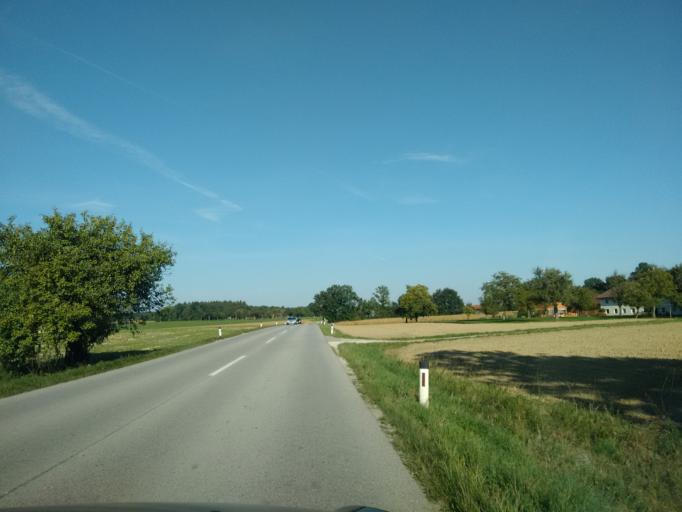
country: AT
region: Upper Austria
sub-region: Politischer Bezirk Linz-Land
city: Horsching
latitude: 48.1481
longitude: 14.1905
